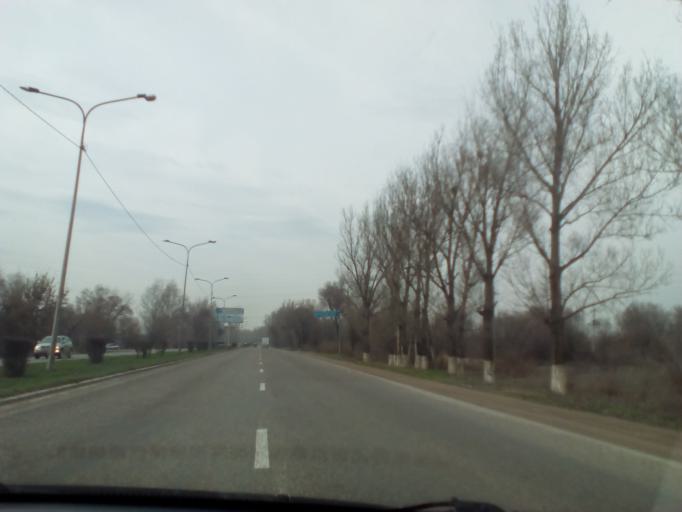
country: KZ
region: Almaty Oblysy
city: Burunday
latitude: 43.2220
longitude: 76.6196
